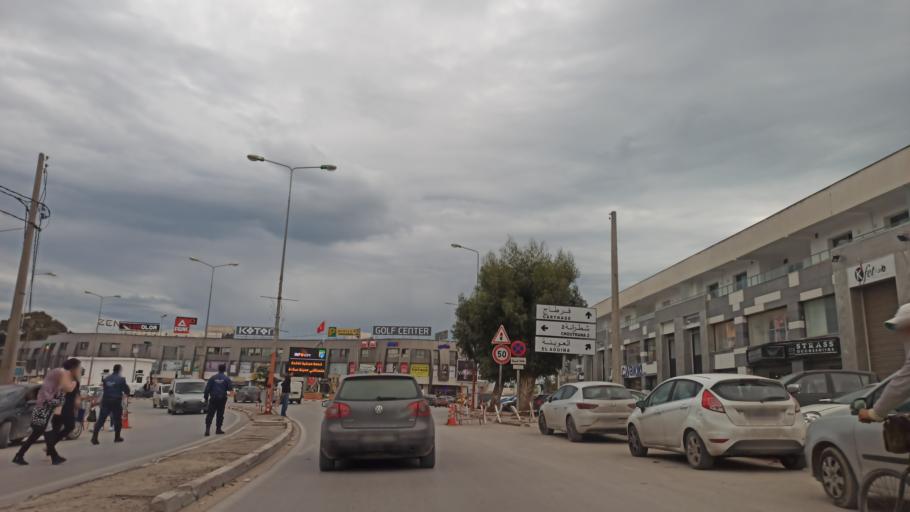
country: TN
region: Ariana
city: Ariana
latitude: 36.8749
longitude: 10.2444
